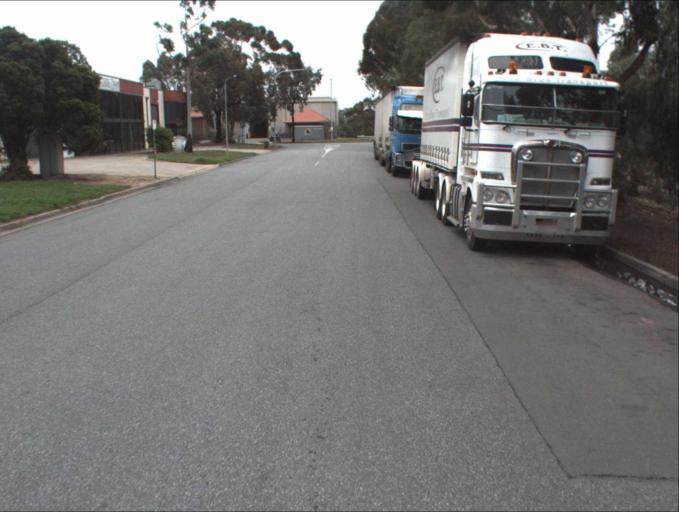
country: AU
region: South Australia
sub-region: Port Adelaide Enfield
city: Blair Athol
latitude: -34.8481
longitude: 138.5690
